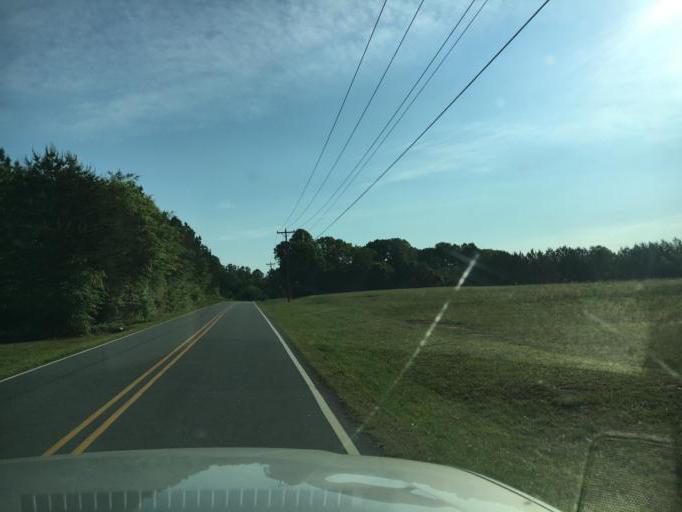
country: US
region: North Carolina
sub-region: Rutherford County
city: Rutherfordton
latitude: 35.3707
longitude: -81.9739
